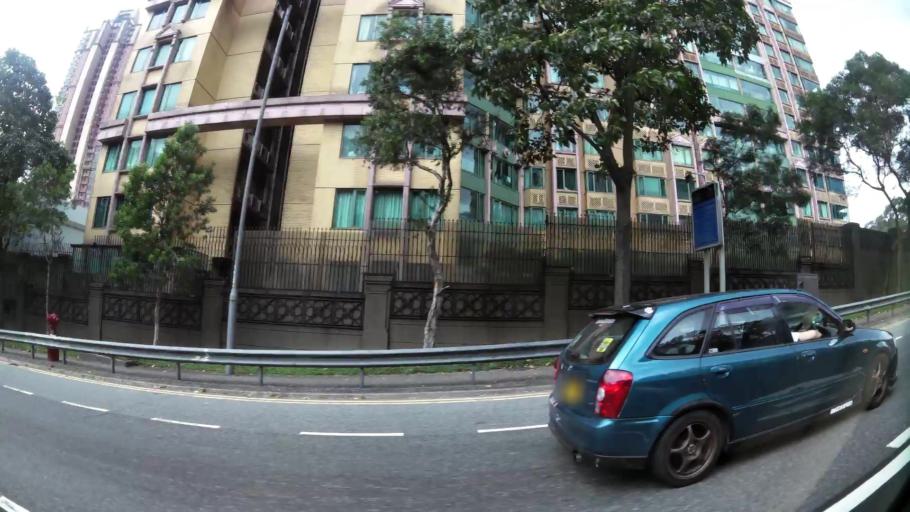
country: HK
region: Wong Tai Sin
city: Wong Tai Sin
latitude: 22.3436
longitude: 114.1832
